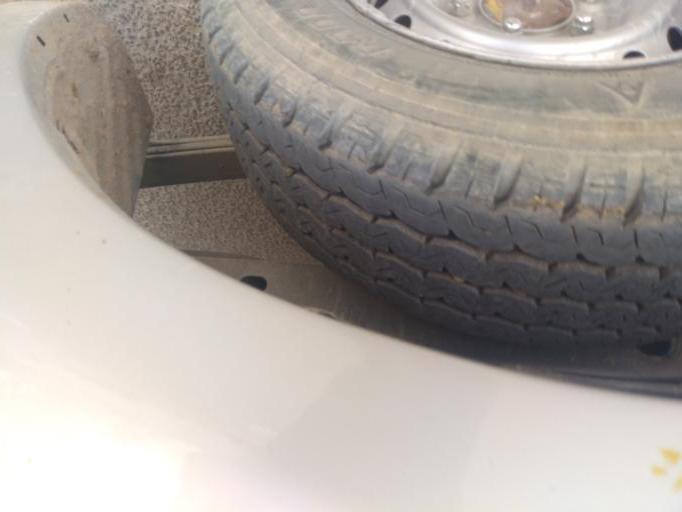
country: TN
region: Al Qayrawan
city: Kairouan
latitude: 35.6699
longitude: 10.0821
